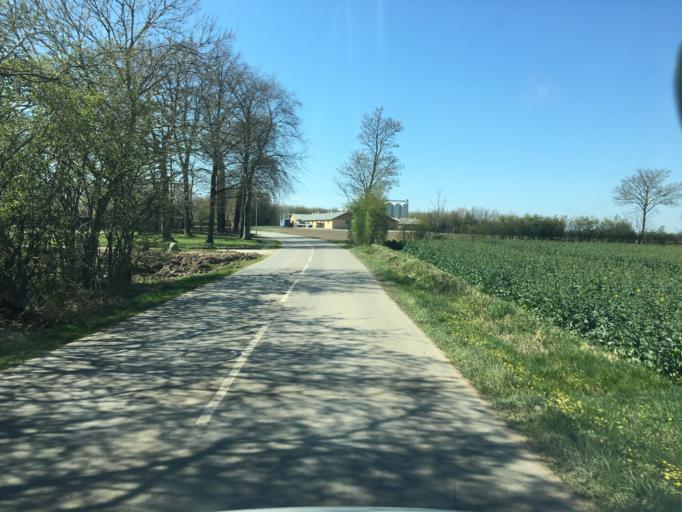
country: DK
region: South Denmark
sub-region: Sonderborg Kommune
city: Dybbol
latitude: 54.9521
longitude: 9.7159
